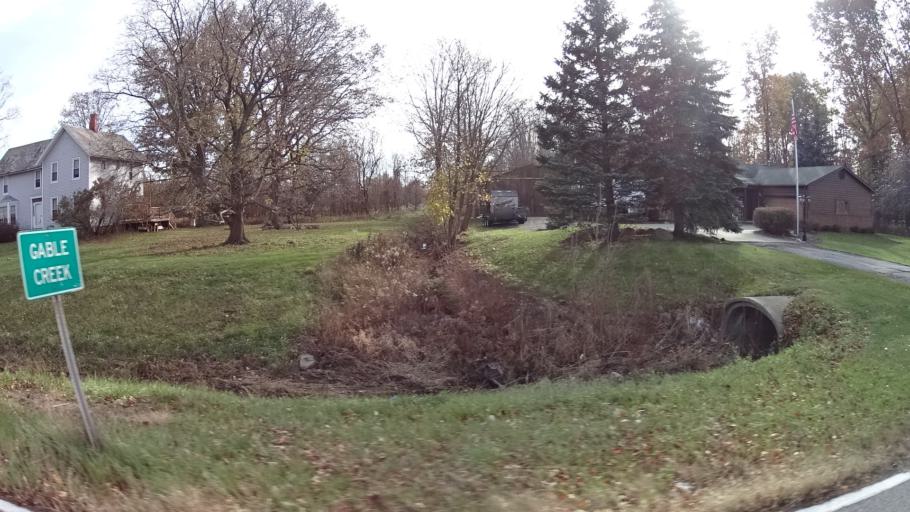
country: US
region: Ohio
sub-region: Lorain County
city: Avon Lake
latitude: 41.4928
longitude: -81.9843
